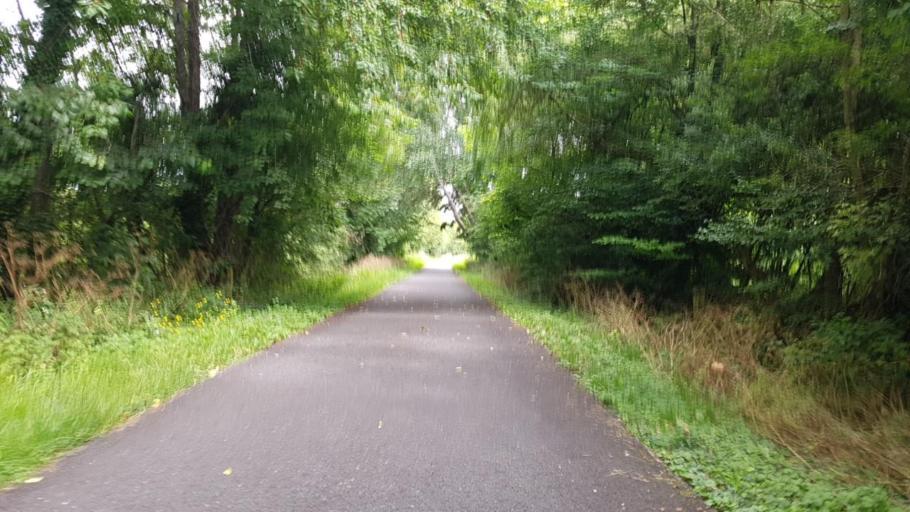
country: FR
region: Picardie
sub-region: Departement de l'Aisne
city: Esqueheries
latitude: 49.8990
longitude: 3.7444
